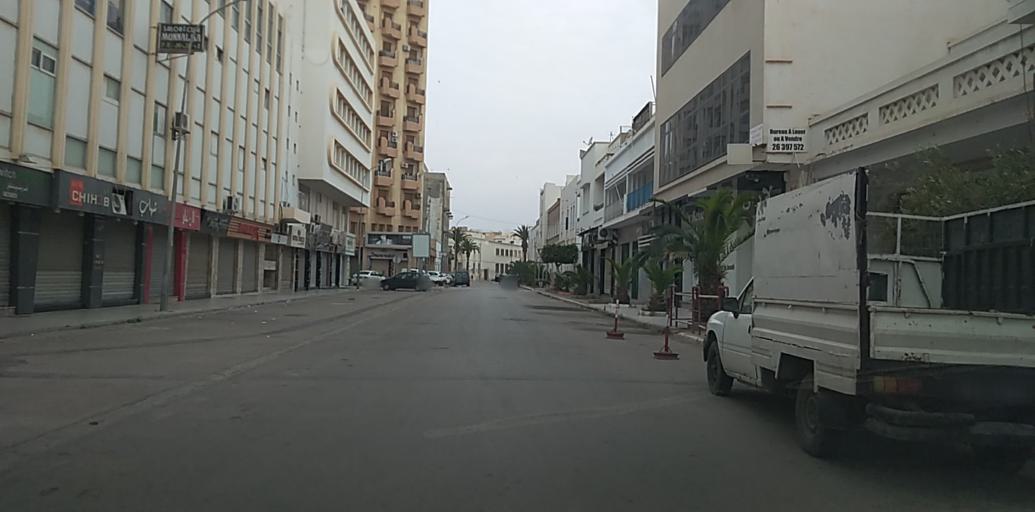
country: TN
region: Safaqis
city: Sfax
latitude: 34.7309
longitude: 10.7643
